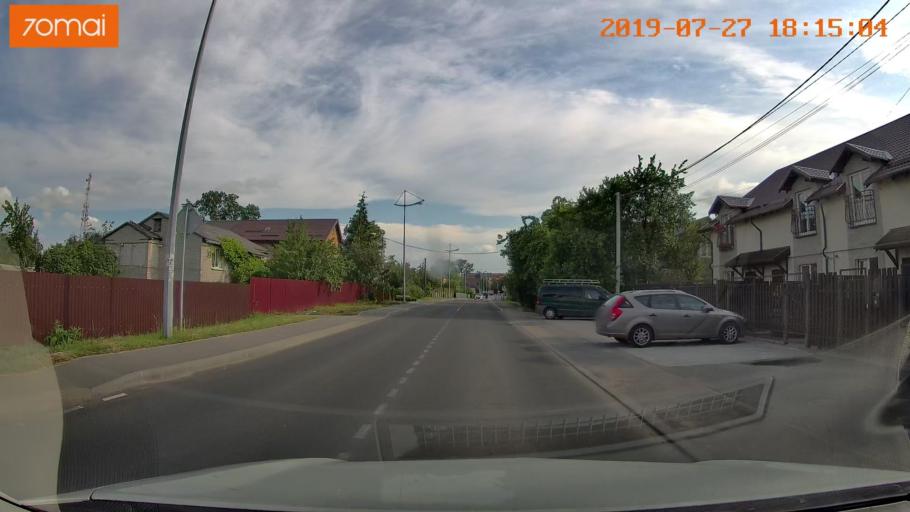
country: RU
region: Kaliningrad
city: Bol'shoe Isakovo
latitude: 54.7220
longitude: 20.6005
